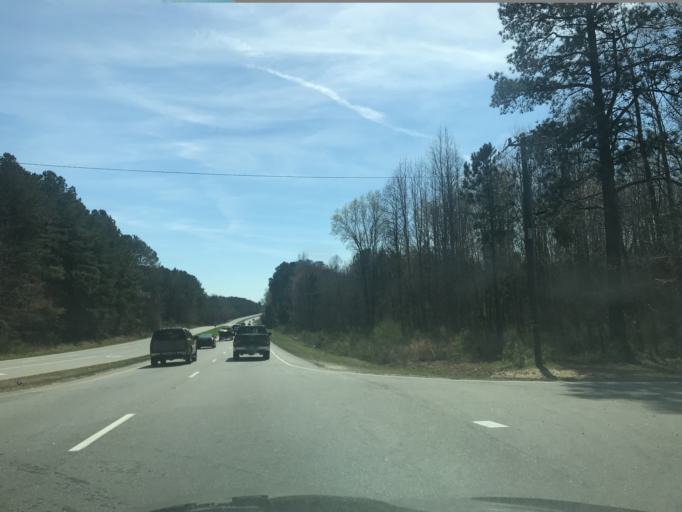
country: US
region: North Carolina
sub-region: Wake County
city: Fuquay-Varina
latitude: 35.6487
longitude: -78.7082
